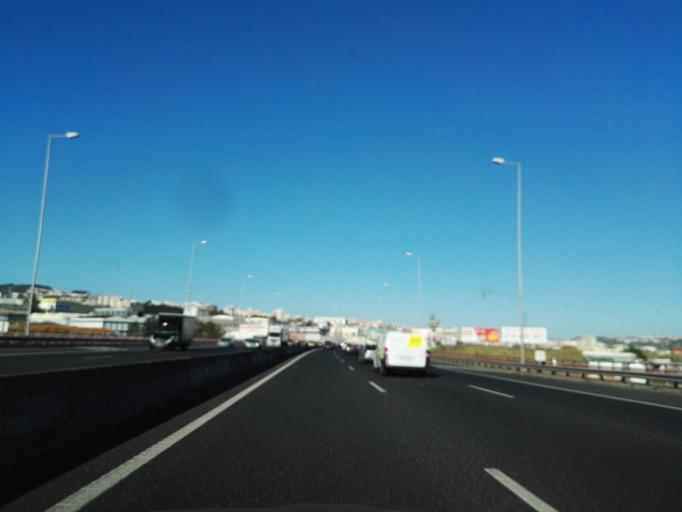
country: PT
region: Lisbon
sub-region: Odivelas
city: Pontinha
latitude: 38.7760
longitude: -9.1962
